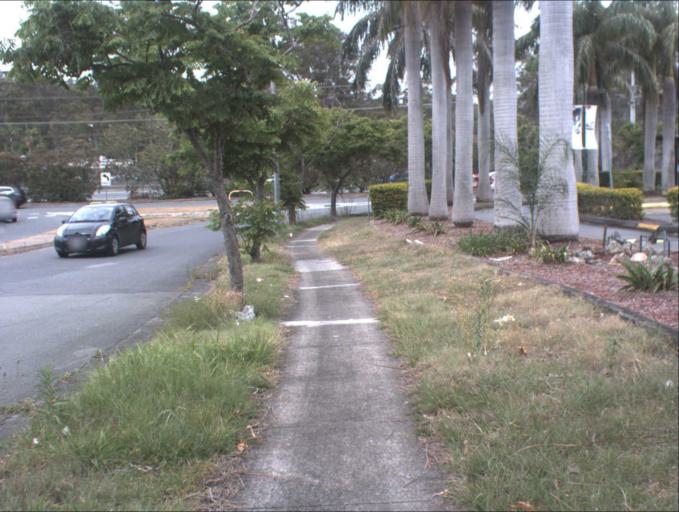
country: AU
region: Queensland
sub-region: Logan
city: Slacks Creek
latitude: -27.6592
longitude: 153.1689
